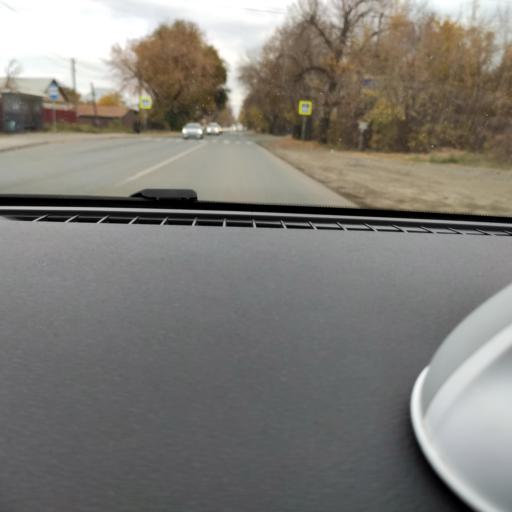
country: RU
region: Samara
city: Smyshlyayevka
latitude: 53.2342
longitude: 50.3126
